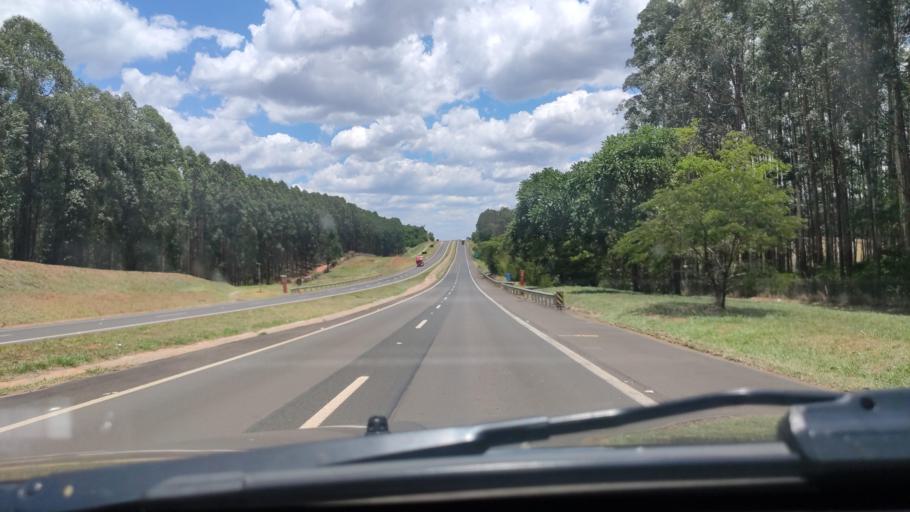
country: BR
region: Sao Paulo
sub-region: Duartina
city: Duartina
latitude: -22.4918
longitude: -49.2533
